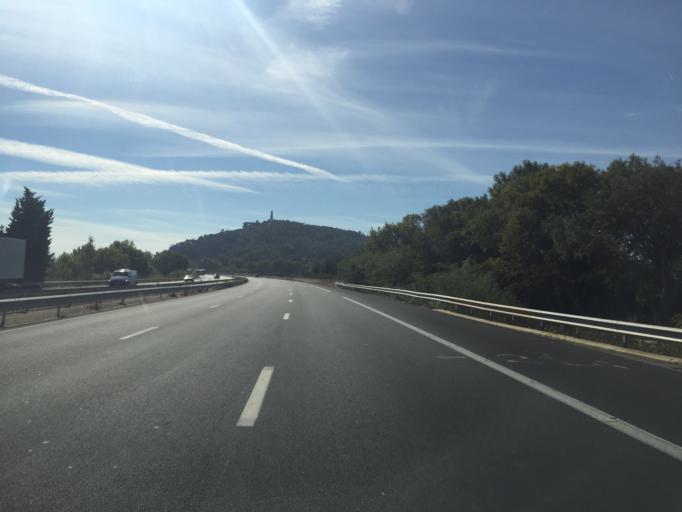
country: FR
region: Provence-Alpes-Cote d'Azur
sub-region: Departement des Bouches-du-Rhone
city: Orgon
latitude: 43.7975
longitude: 5.0399
